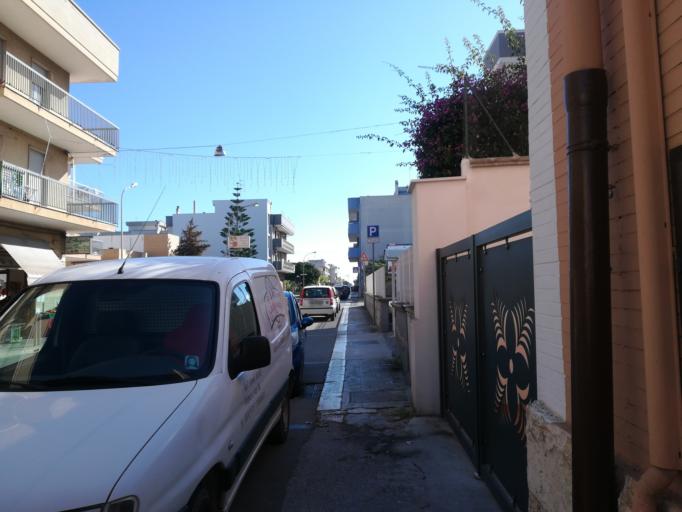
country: IT
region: Apulia
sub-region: Provincia di Bari
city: Polignano a Mare
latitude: 40.9918
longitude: 17.2256
